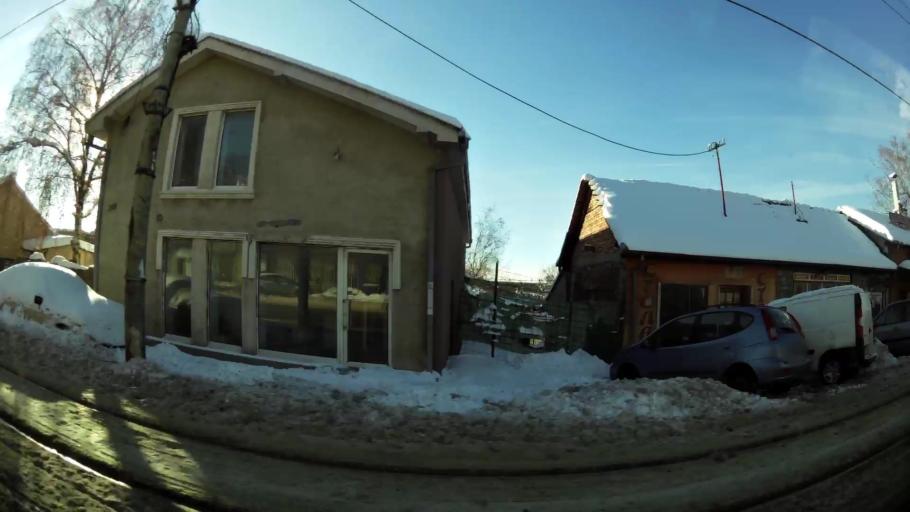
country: RS
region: Central Serbia
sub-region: Belgrade
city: Palilula
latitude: 44.7926
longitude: 20.5071
